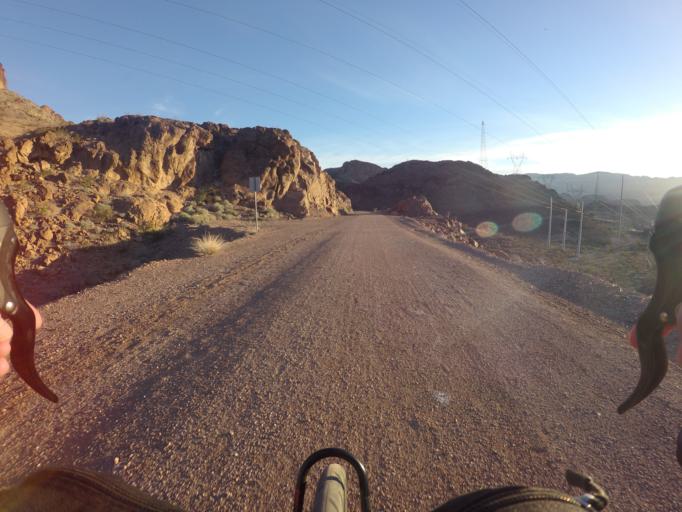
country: US
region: Nevada
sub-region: Clark County
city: Boulder City
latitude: 36.0168
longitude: -114.7514
